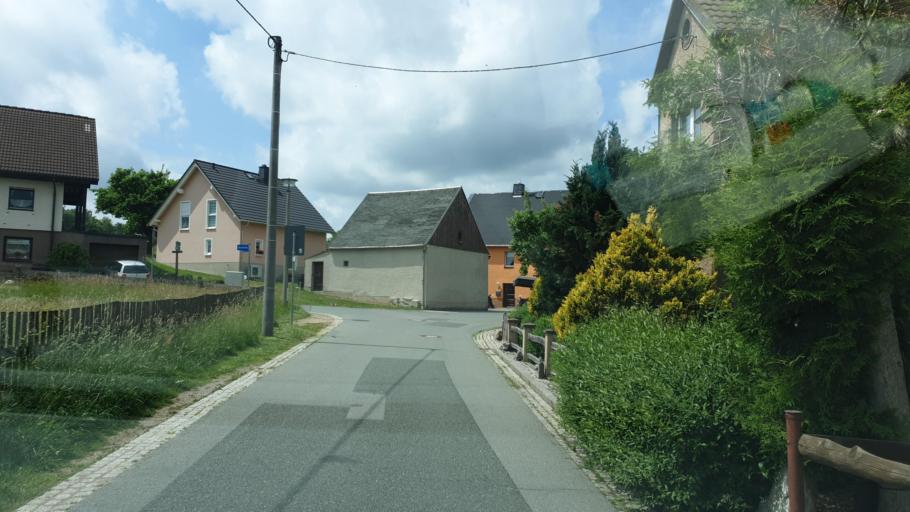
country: DE
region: Saxony
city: Marienberg
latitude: 50.6663
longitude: 13.1483
